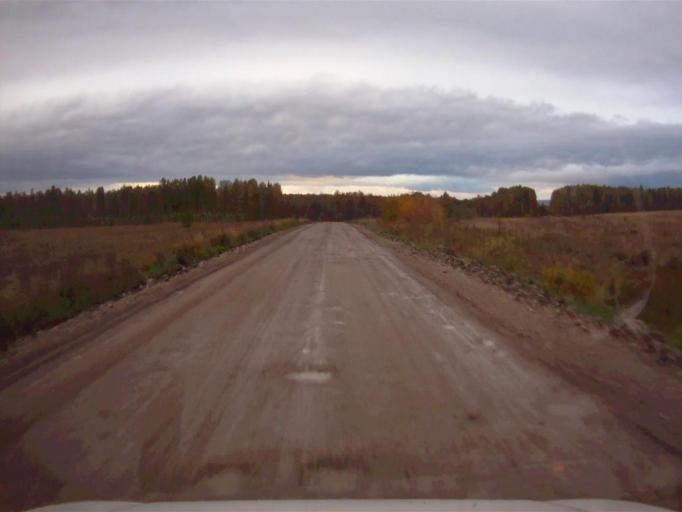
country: RU
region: Sverdlovsk
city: Mikhaylovsk
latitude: 56.1880
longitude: 59.1874
